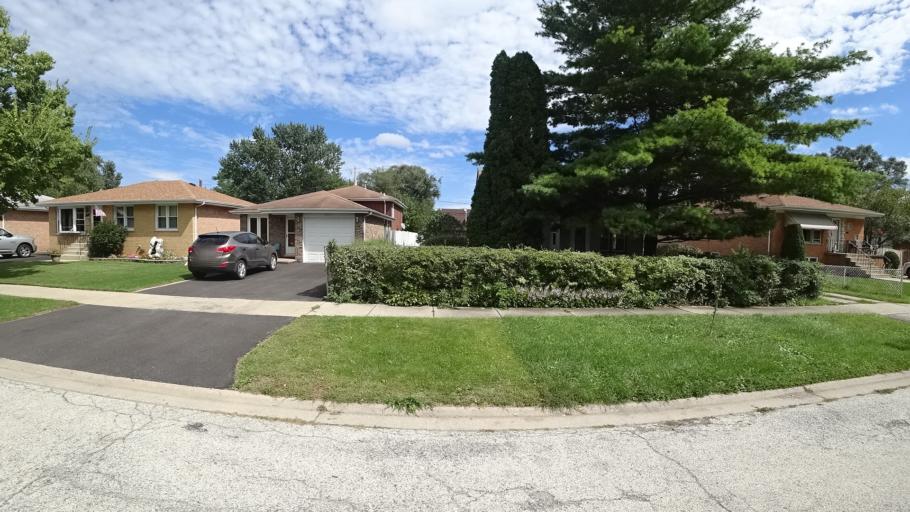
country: US
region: Illinois
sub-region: Cook County
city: Chicago Ridge
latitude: 41.7149
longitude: -87.7882
